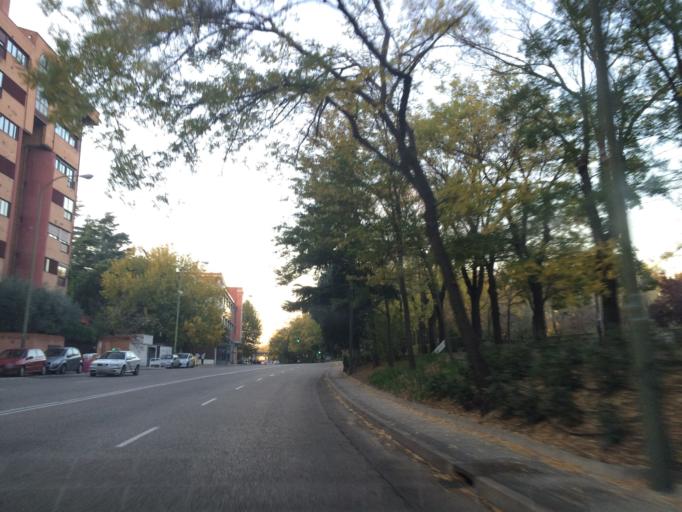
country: ES
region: Madrid
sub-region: Provincia de Madrid
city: Moncloa-Aravaca
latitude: 40.4301
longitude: -3.7310
